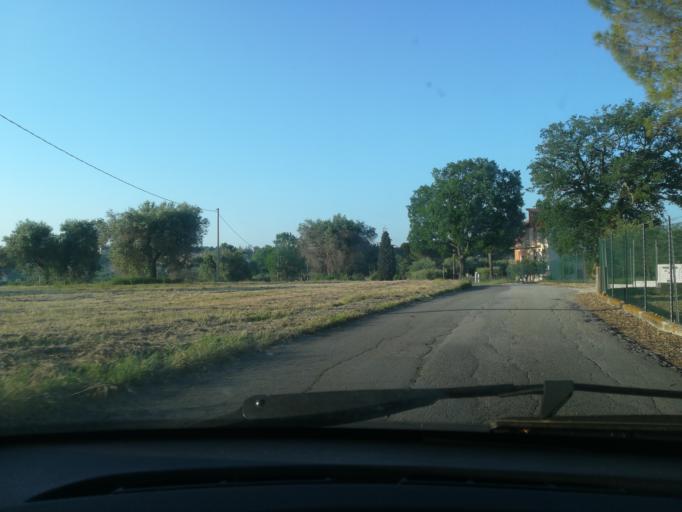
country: IT
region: The Marches
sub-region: Provincia di Macerata
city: Piediripa
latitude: 43.2830
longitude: 13.4700
